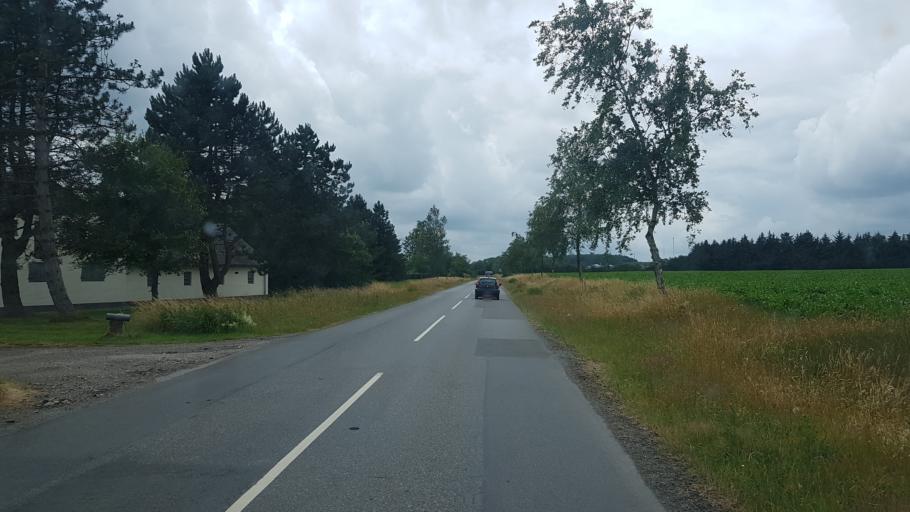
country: DK
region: South Denmark
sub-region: Kolding Kommune
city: Lunderskov
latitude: 55.4617
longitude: 9.2882
